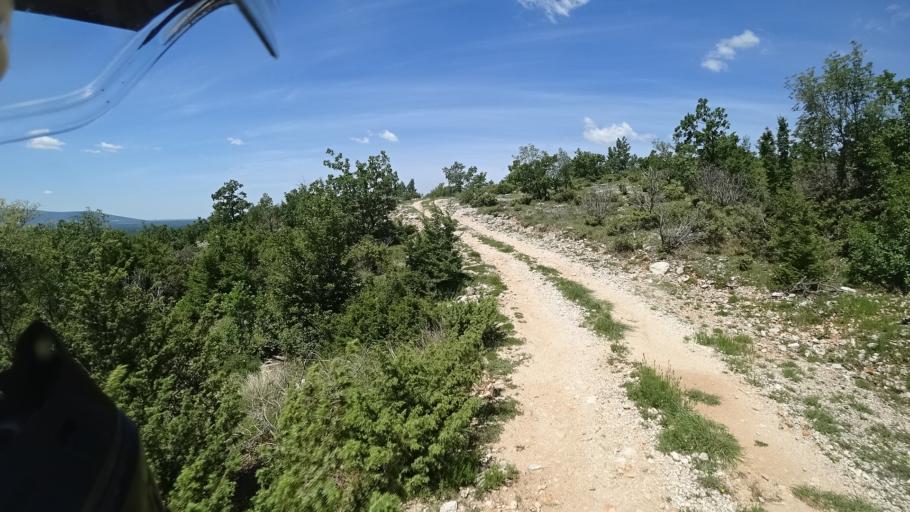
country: HR
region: Sibensko-Kniniska
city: Knin
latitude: 44.0301
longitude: 16.2856
